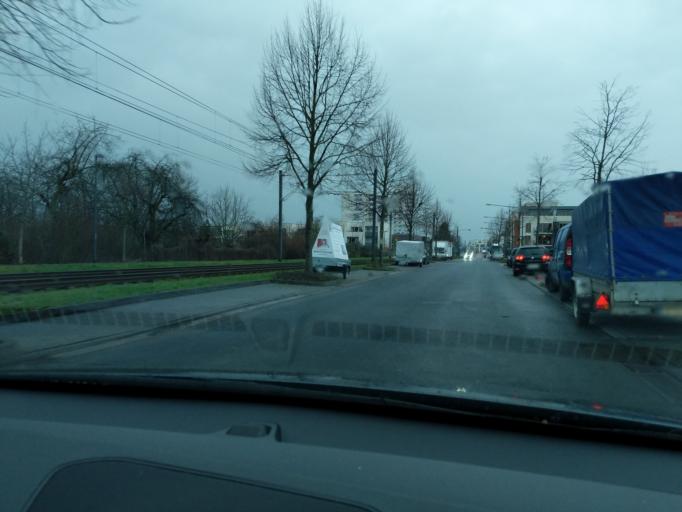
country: DE
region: Hesse
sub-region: Regierungsbezirk Darmstadt
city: Frankfurt am Main
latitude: 50.1506
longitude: 8.7003
